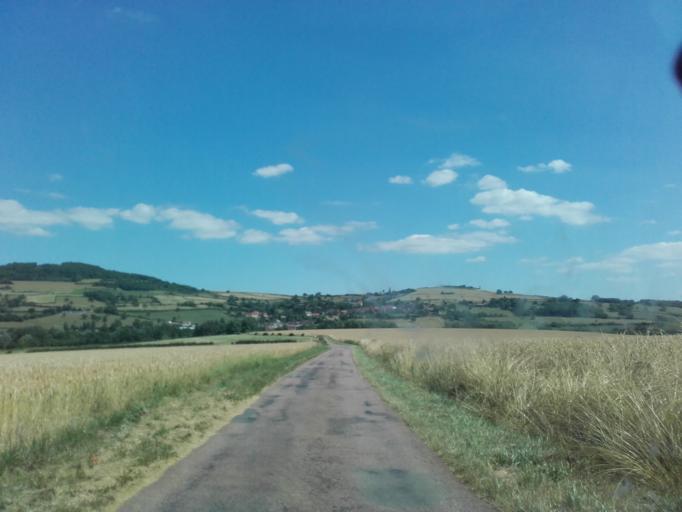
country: FR
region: Bourgogne
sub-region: Departement de Saone-et-Loire
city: Saint-Leger-sur-Dheune
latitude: 46.8837
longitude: 4.6525
